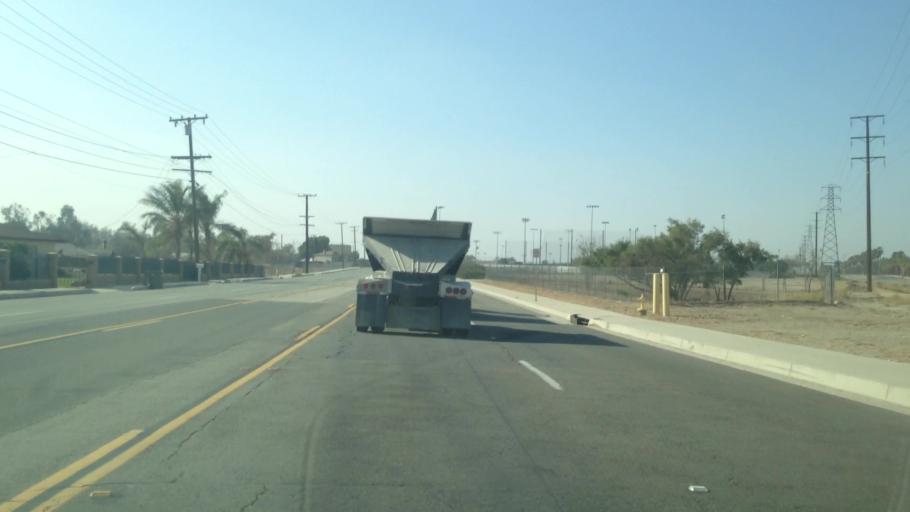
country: US
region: California
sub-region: Riverside County
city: Mira Loma
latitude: 34.0038
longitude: -117.5103
